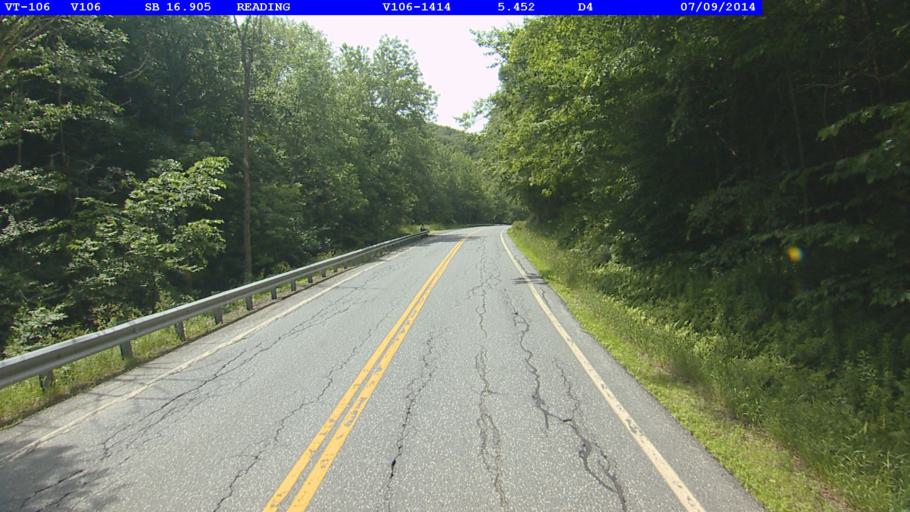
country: US
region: Vermont
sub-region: Windsor County
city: Woodstock
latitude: 43.5138
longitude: -72.5485
